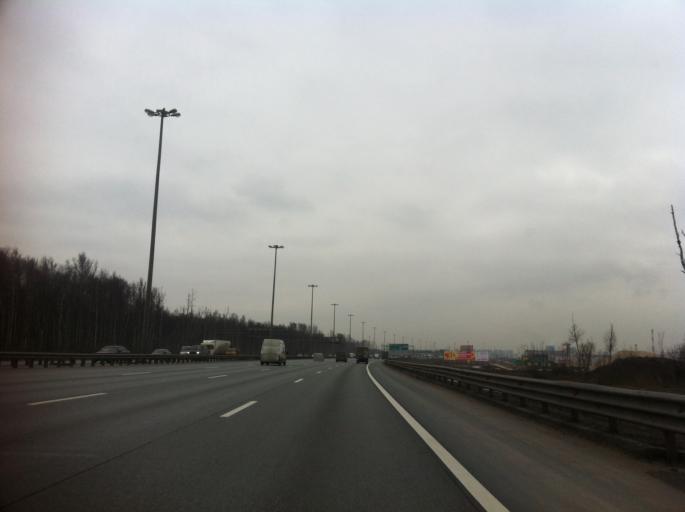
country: RU
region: Leningrad
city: Rybatskoye
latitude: 59.9046
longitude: 30.5261
